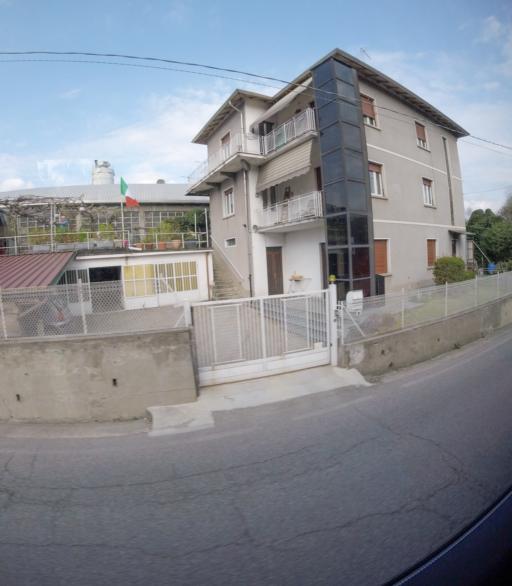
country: IT
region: Piedmont
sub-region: Provincia di Novara
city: Bolzano Novarese
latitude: 45.7570
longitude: 8.4319
